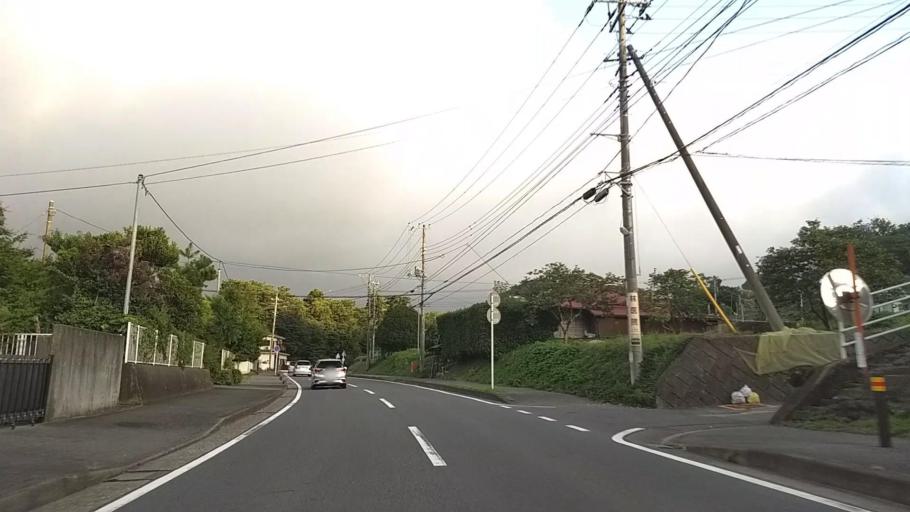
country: JP
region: Kanagawa
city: Atsugi
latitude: 35.4756
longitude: 139.2838
